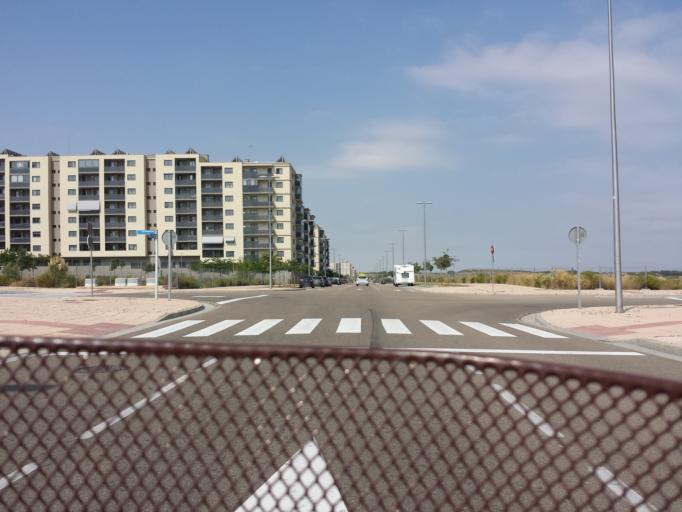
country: ES
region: Aragon
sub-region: Provincia de Zaragoza
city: Montecanal
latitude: 41.6233
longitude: -0.9503
